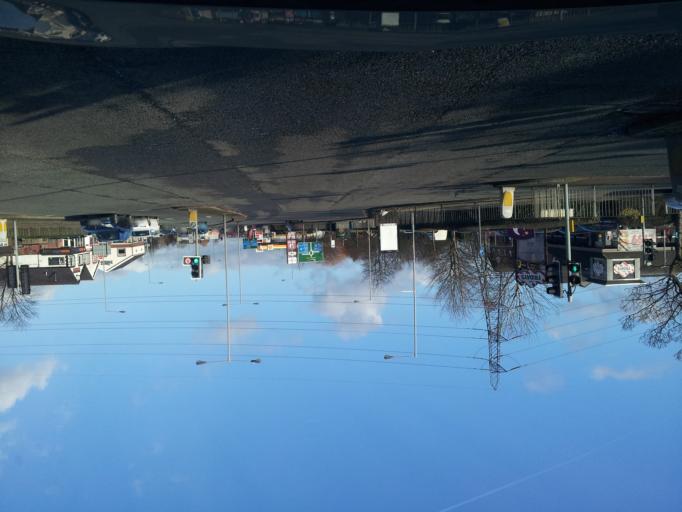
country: GB
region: England
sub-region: Borough of Bury
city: Prestwich
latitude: 53.5364
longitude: -2.2879
